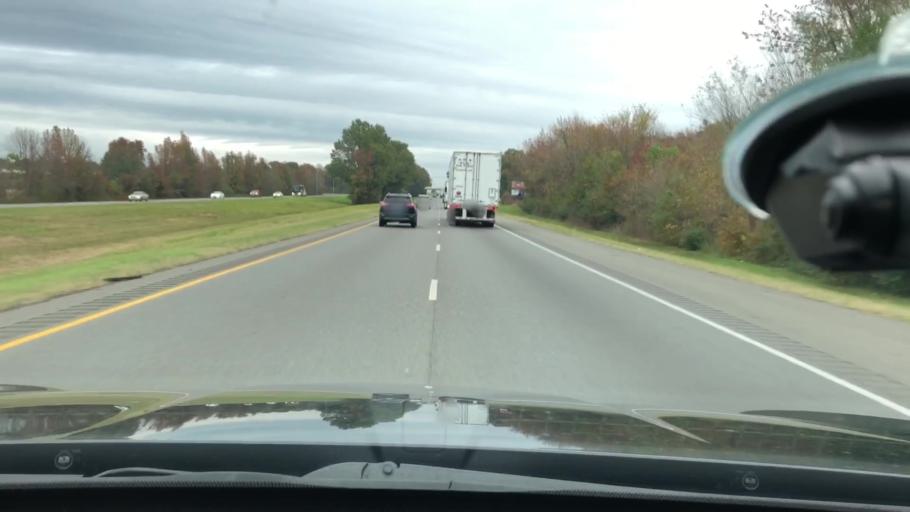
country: US
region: Arkansas
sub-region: Hempstead County
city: Hope
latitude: 33.6771
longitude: -93.6170
